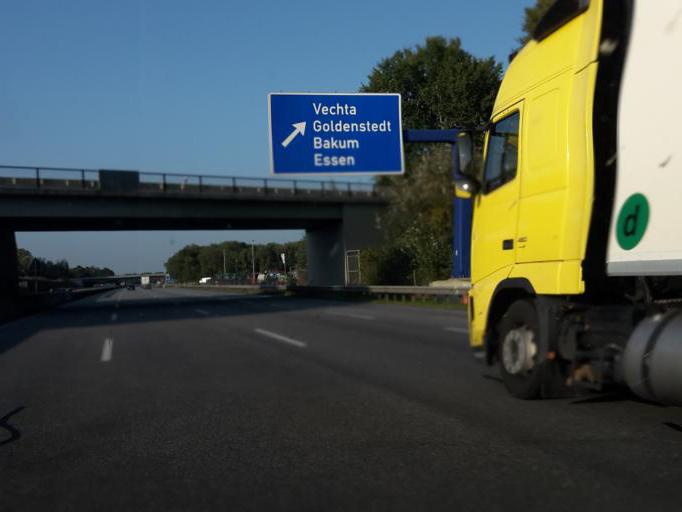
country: DE
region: Lower Saxony
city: Bakum
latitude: 52.7202
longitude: 8.1729
